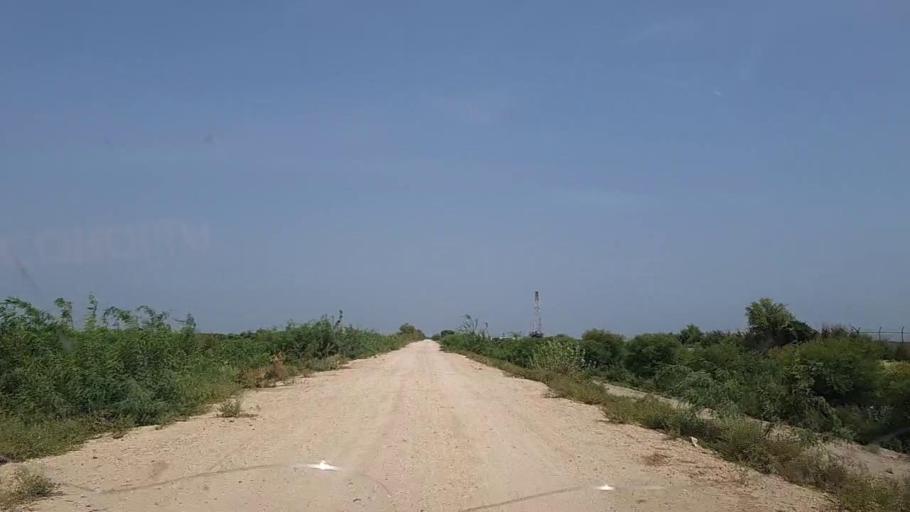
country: PK
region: Sindh
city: Ghotki
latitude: 28.1180
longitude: 69.3803
